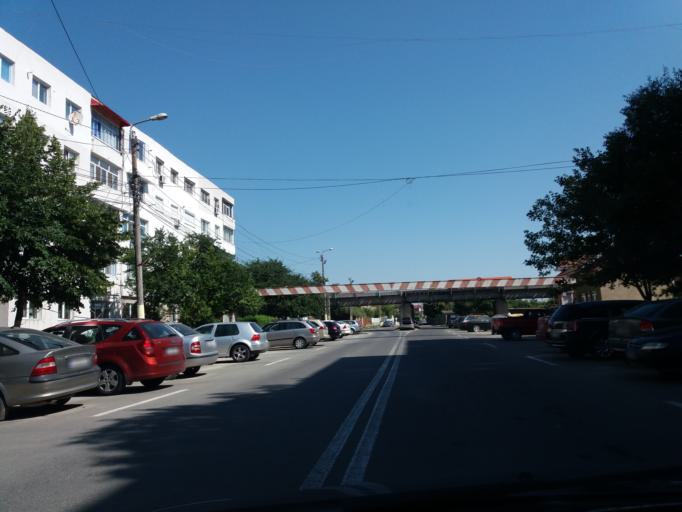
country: RO
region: Constanta
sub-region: Comuna Navodari
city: Navodari
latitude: 44.3263
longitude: 28.6104
